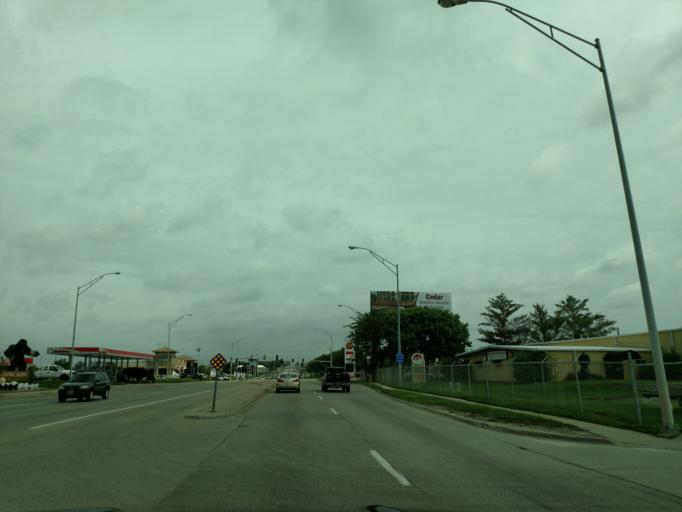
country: US
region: Nebraska
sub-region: Douglas County
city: Ralston
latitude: 41.2037
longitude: -96.0237
